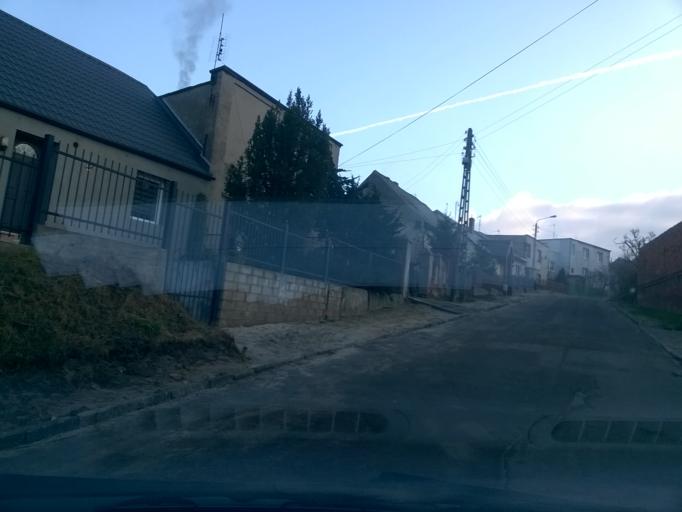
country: PL
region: Kujawsko-Pomorskie
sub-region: Powiat nakielski
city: Kcynia
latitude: 52.9940
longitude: 17.4874
